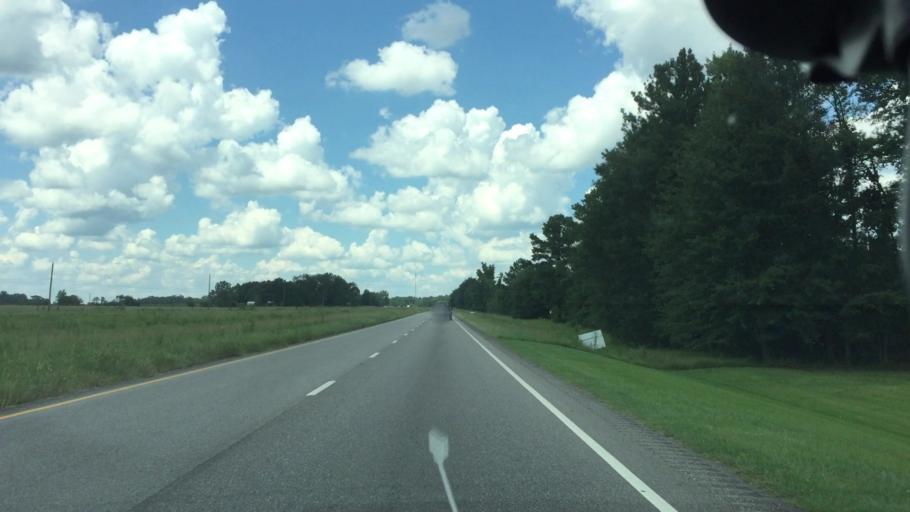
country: US
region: Alabama
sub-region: Montgomery County
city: Taylor
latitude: 32.0265
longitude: -86.0318
